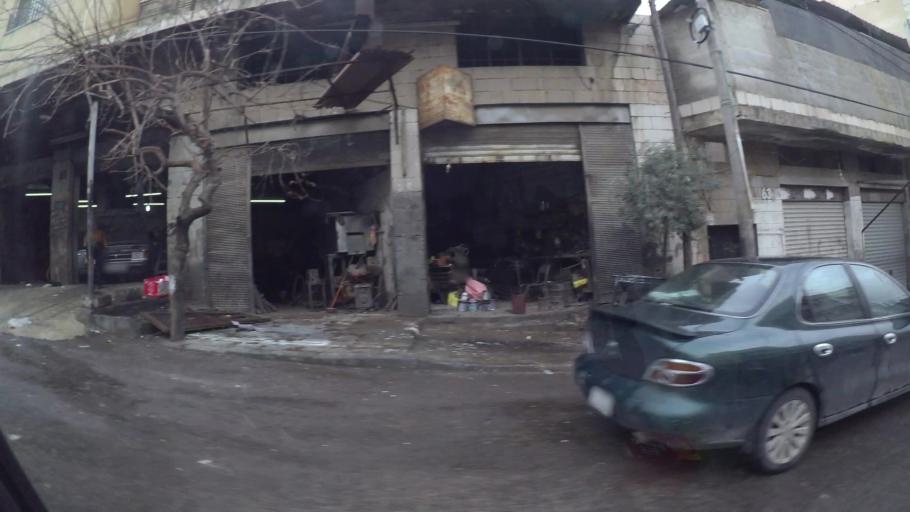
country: JO
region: Amman
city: Al Jubayhah
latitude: 32.0314
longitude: 35.8365
